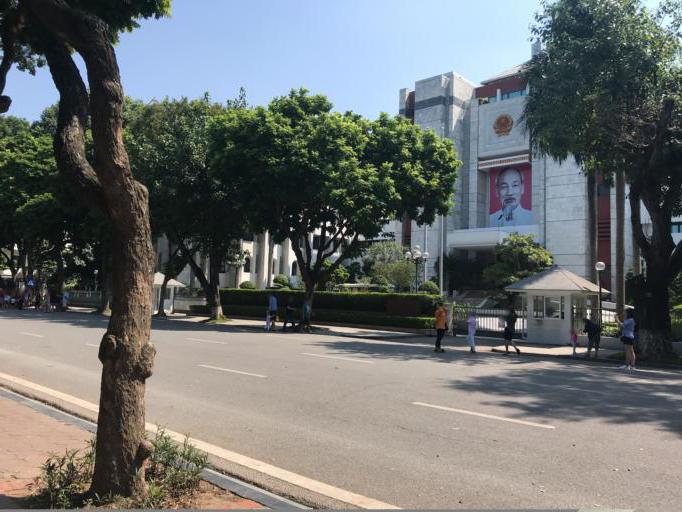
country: VN
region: Ha Noi
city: Hoan Kiem
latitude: 21.0281
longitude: 105.8536
